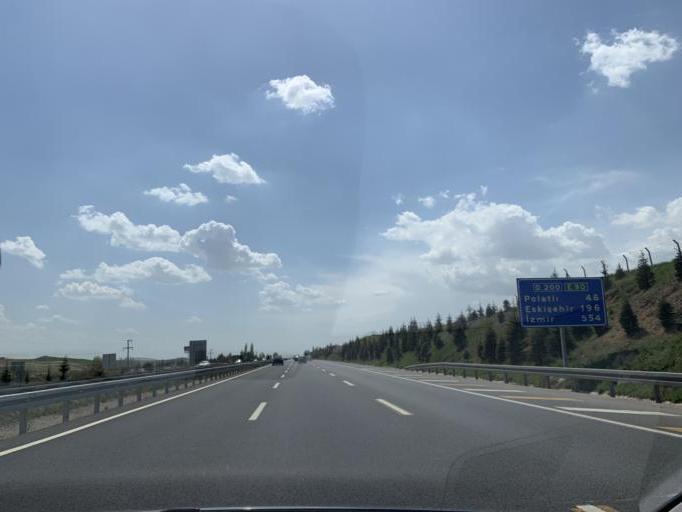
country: TR
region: Ankara
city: Etimesgut
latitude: 39.8108
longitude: 32.5547
